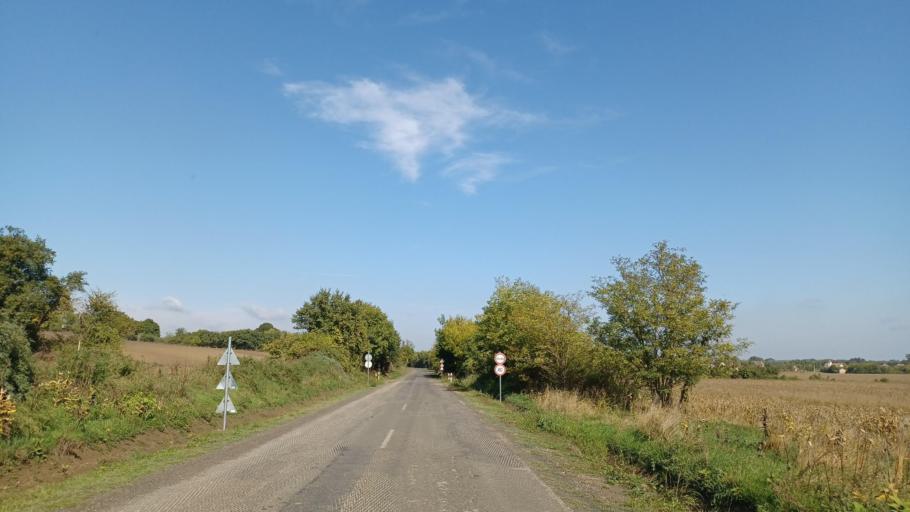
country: HU
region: Tolna
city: Nagydorog
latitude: 46.5946
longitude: 18.5958
